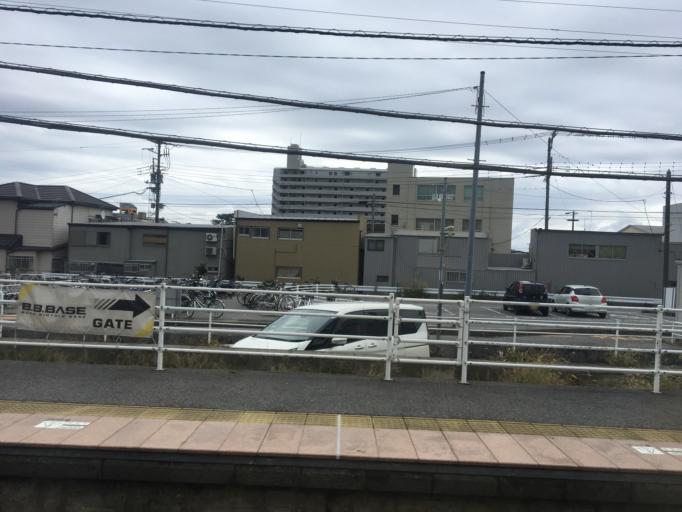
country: JP
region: Chiba
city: Kawaguchi
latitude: 35.1082
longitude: 140.1042
